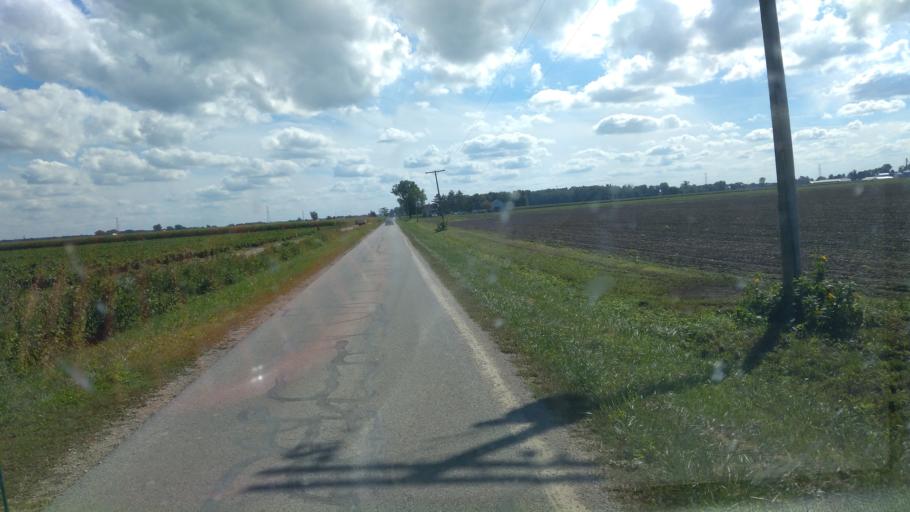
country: US
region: Ohio
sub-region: Ottawa County
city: Port Clinton
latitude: 41.4037
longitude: -82.8824
